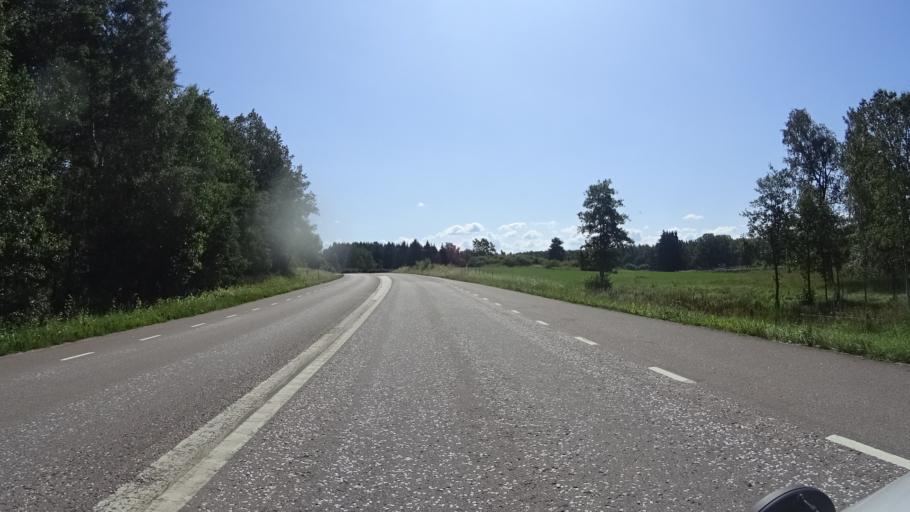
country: SE
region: OEstergoetland
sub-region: Vadstena Kommun
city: Herrestad
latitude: 58.3045
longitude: 14.9175
